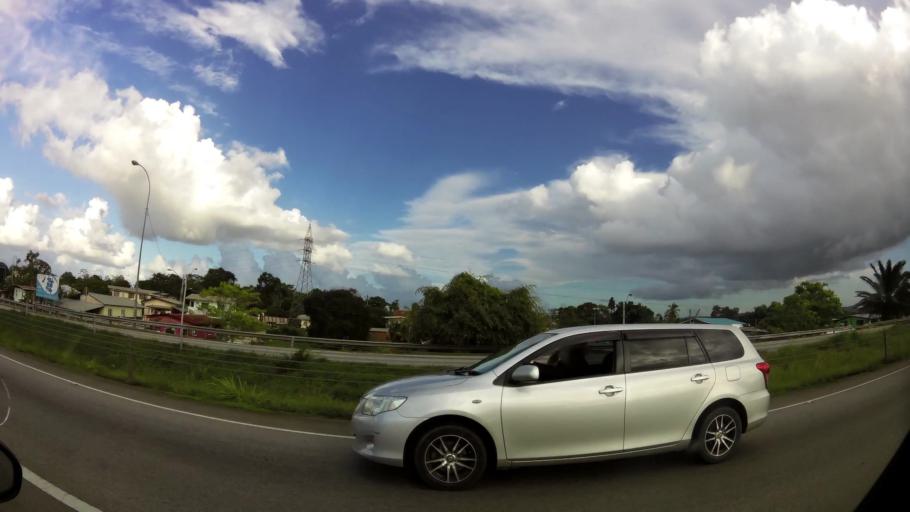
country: TT
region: Chaguanas
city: Chaguanas
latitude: 10.4621
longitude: -61.4105
